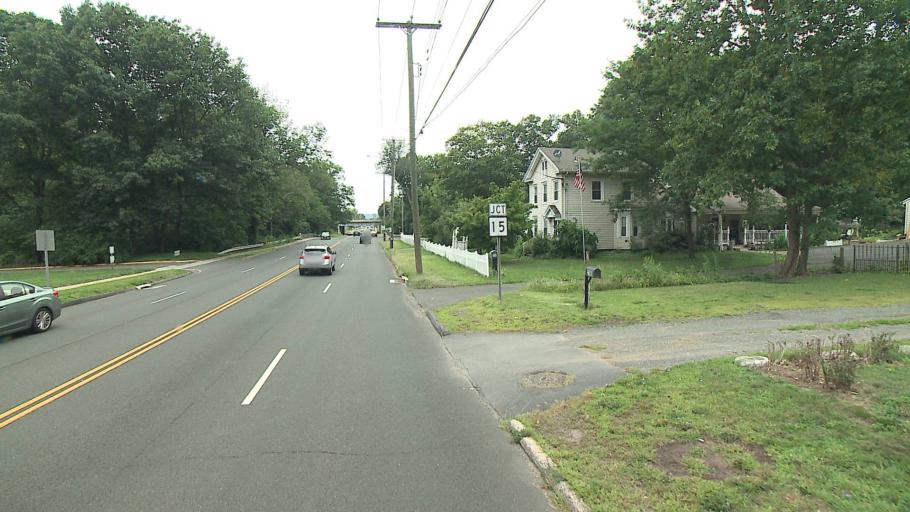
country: US
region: Connecticut
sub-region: New Haven County
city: Hamden
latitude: 41.3769
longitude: -72.9042
